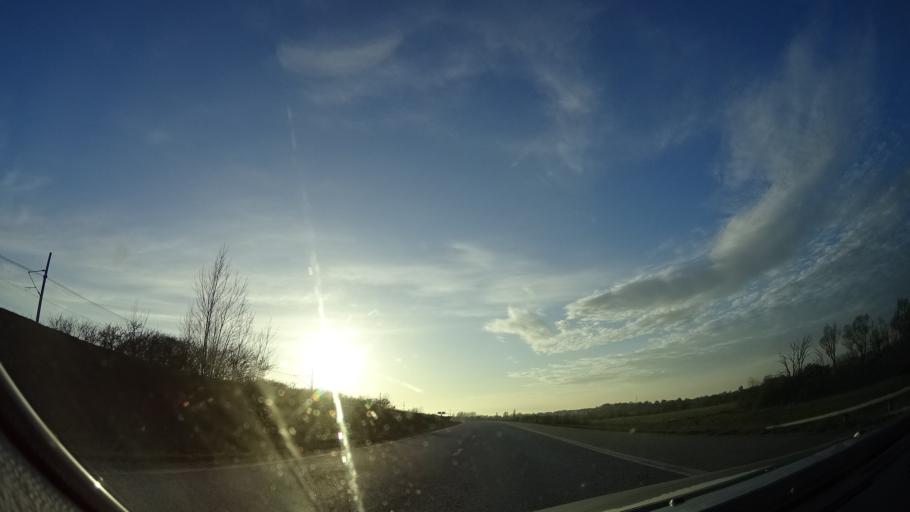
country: SE
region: Skane
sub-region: Malmo
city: Bunkeflostrand
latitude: 55.5625
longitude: 12.9337
